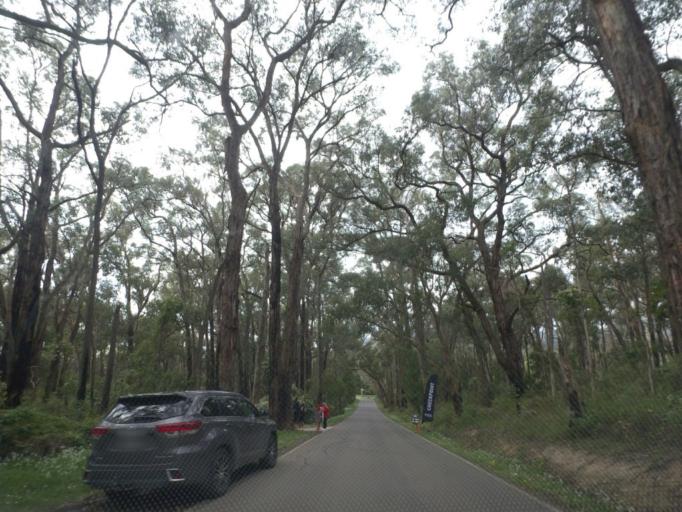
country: AU
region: Victoria
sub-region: Knox
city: The Basin
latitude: -37.8575
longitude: 145.3212
